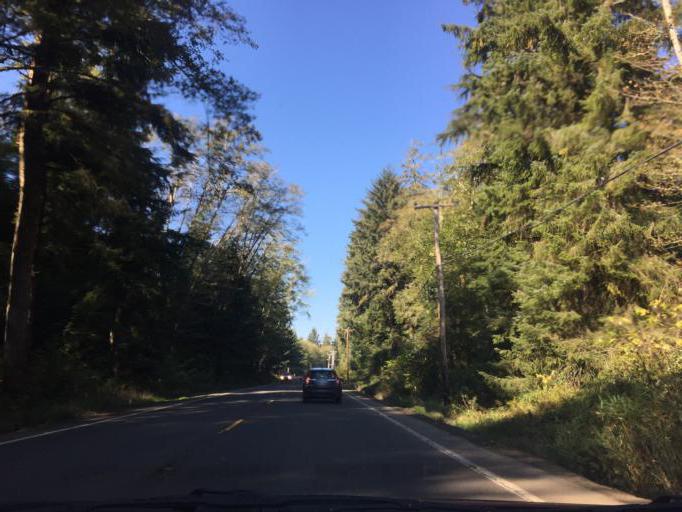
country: US
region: Oregon
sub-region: Clatsop County
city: Cannon Beach
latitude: 45.9047
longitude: -123.8762
